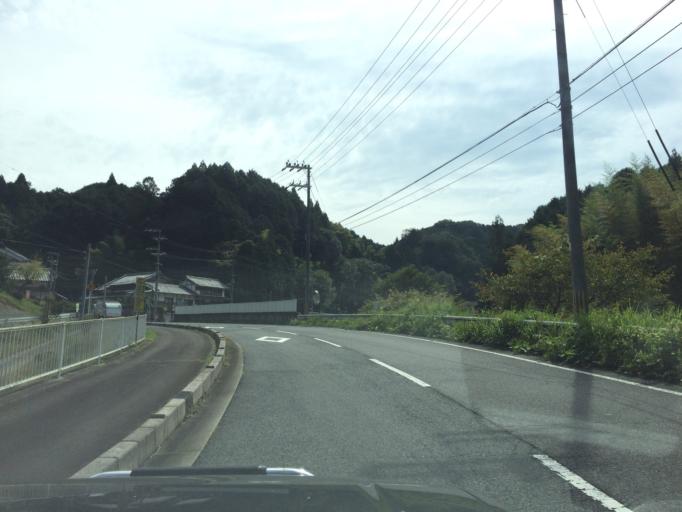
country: JP
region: Mie
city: Nabari
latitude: 34.6787
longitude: 136.0127
